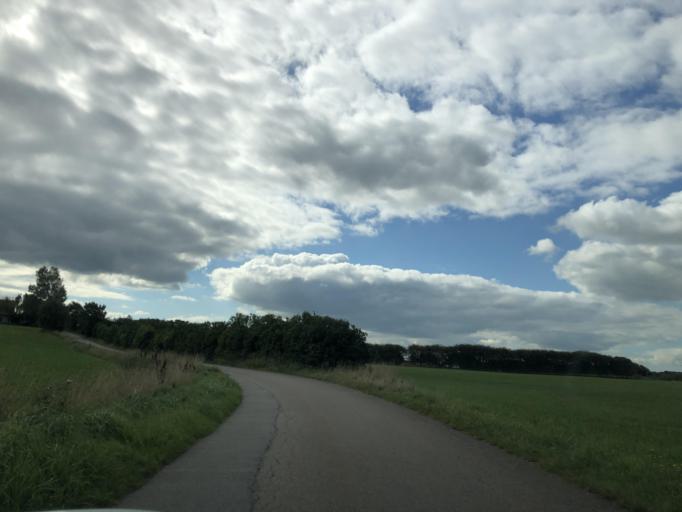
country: DK
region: North Denmark
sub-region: Vesthimmerland Kommune
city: Aars
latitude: 56.8165
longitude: 9.6535
